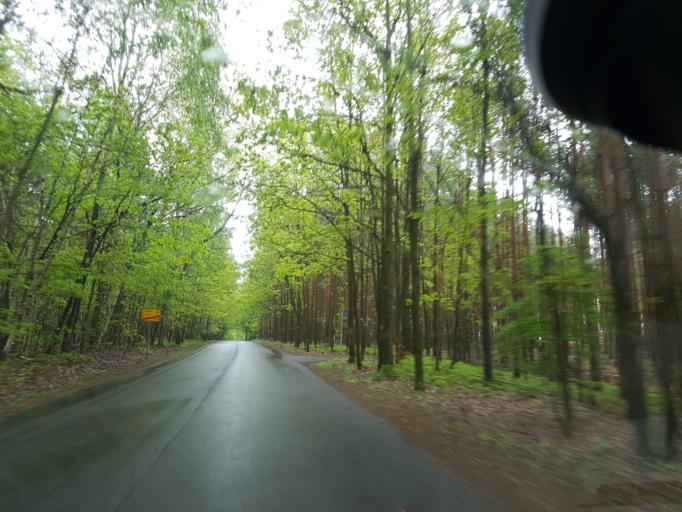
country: DE
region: Brandenburg
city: Tschernitz
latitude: 51.6312
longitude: 14.6023
